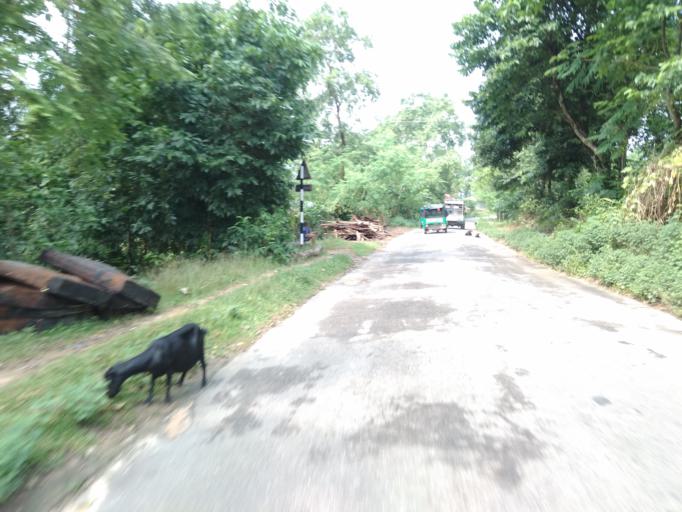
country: BD
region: Chittagong
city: Khagrachhari
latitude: 23.0025
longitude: 92.0114
